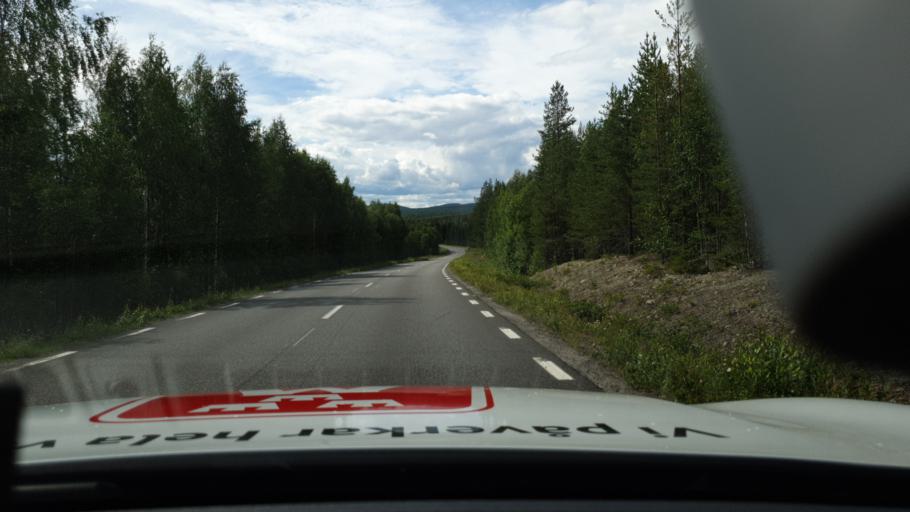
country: SE
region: Norrbotten
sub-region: Bodens Kommun
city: Boden
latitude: 65.9689
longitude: 21.6131
